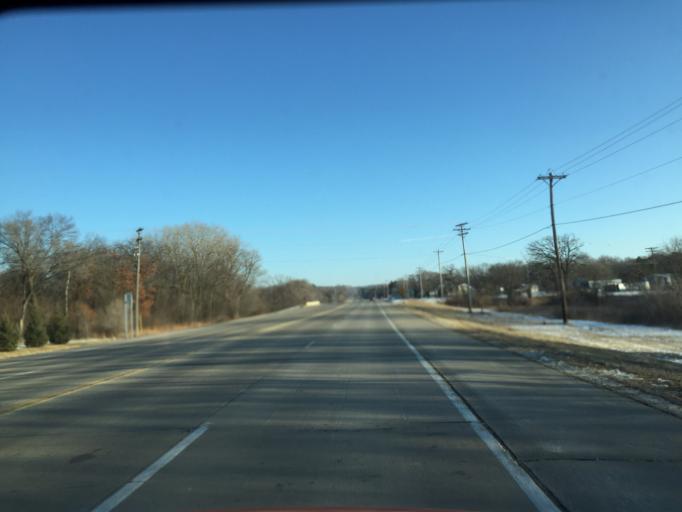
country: US
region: Minnesota
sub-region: Olmsted County
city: Rochester
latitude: 43.9916
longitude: -92.4199
